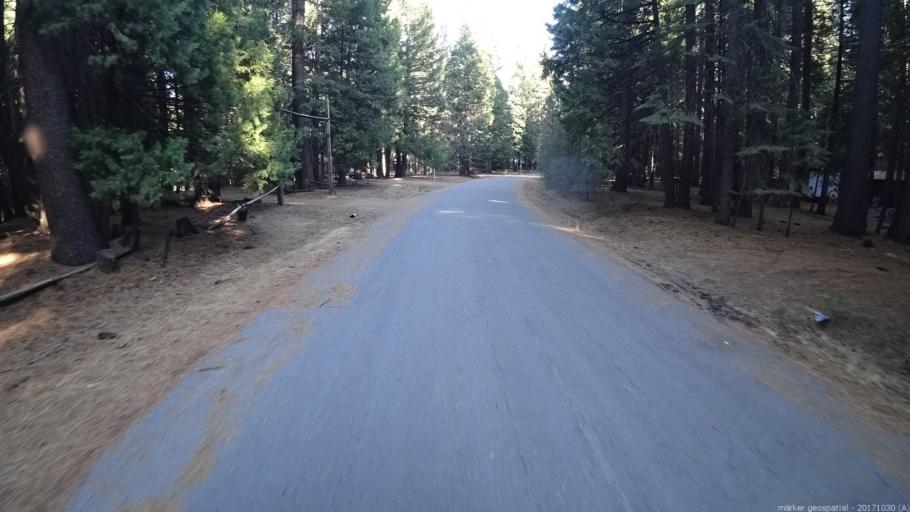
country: US
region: California
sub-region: Shasta County
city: Shingletown
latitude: 40.5551
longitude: -121.7302
